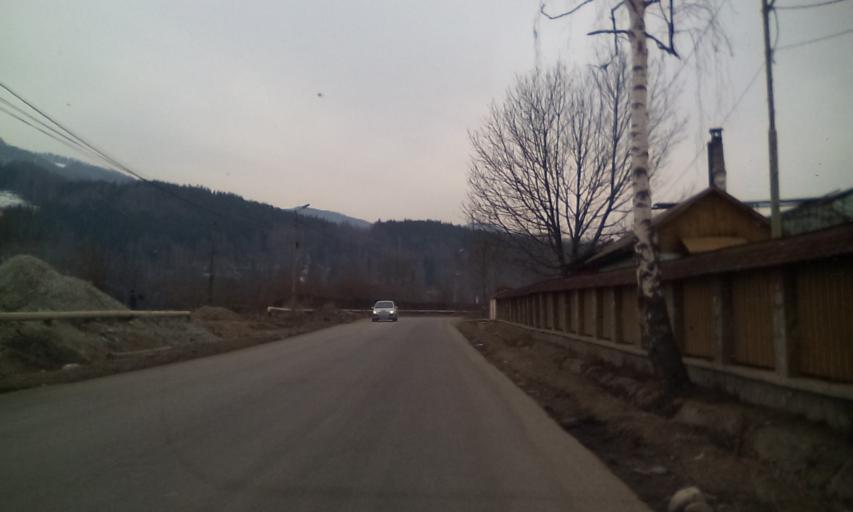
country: RO
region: Hunedoara
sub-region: Comuna Uricani
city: Uricani
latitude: 45.3430
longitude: 23.1745
